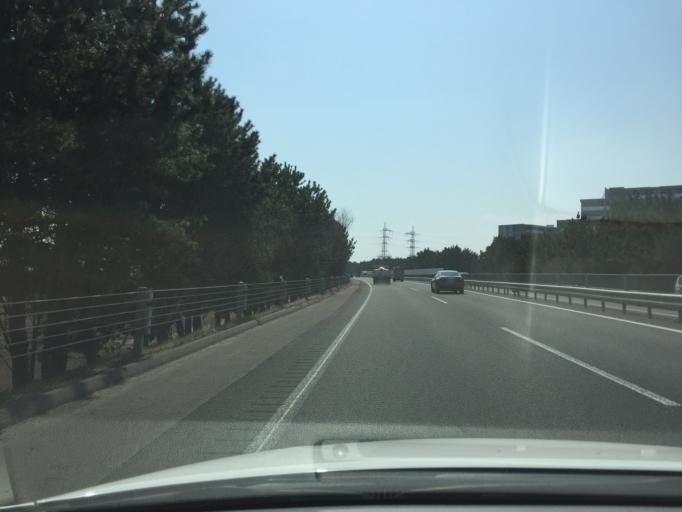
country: JP
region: Miyagi
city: Sendai-shi
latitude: 38.2392
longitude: 140.9520
